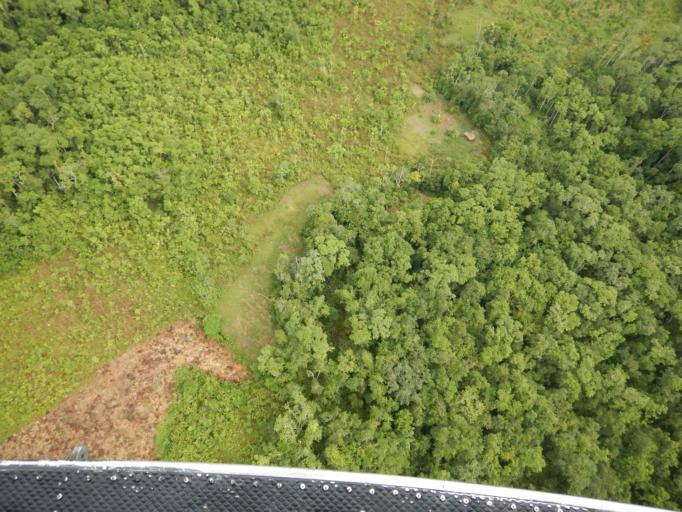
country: BO
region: Cochabamba
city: Chimore
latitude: -16.9699
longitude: -65.0301
